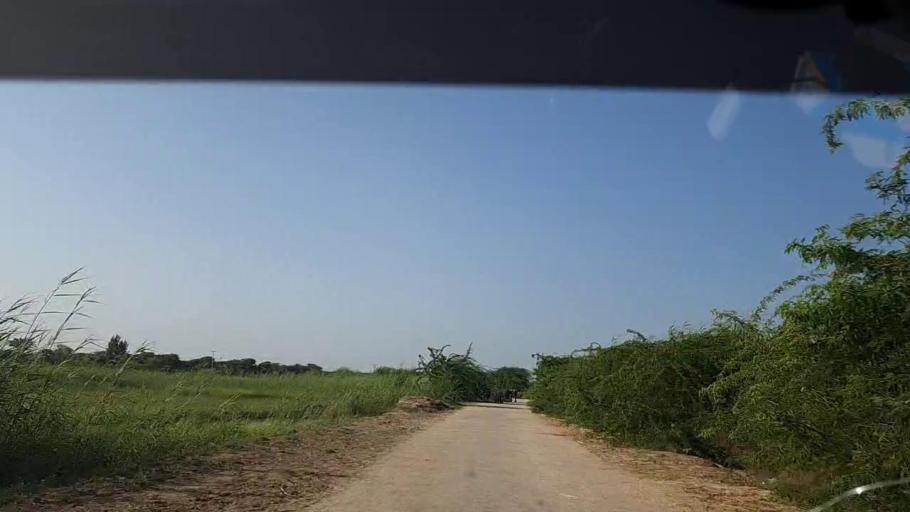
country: PK
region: Sindh
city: Badin
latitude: 24.6869
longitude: 68.8418
